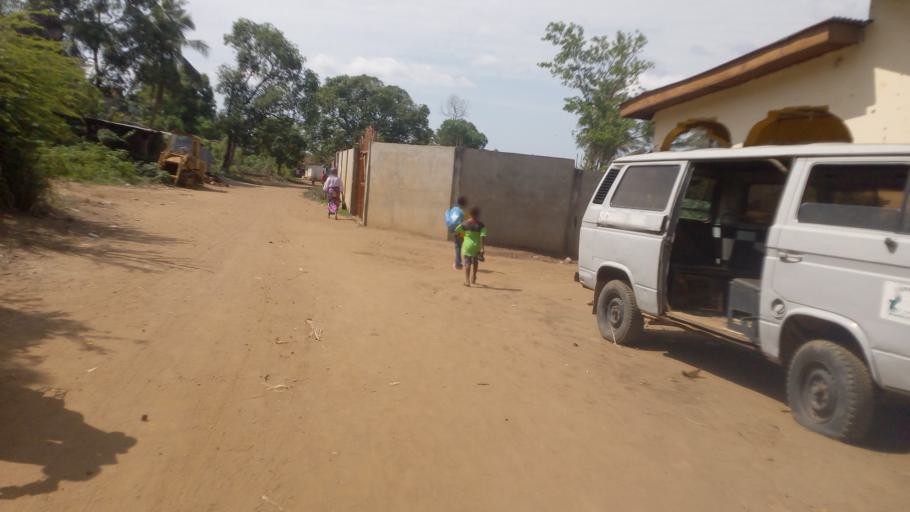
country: SL
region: Western Area
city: Waterloo
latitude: 8.3162
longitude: -13.0724
